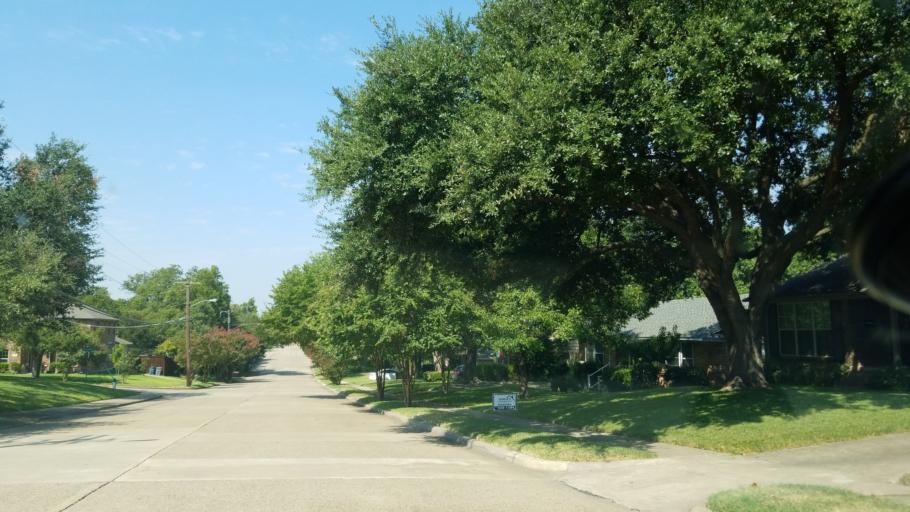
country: US
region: Texas
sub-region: Dallas County
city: Richardson
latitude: 32.8717
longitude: -96.7104
